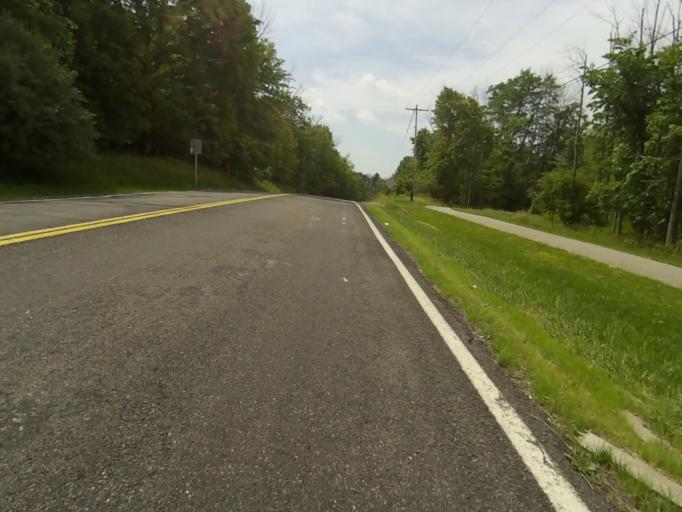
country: US
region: Ohio
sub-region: Summit County
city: Boston Heights
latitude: 41.2801
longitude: -81.5381
